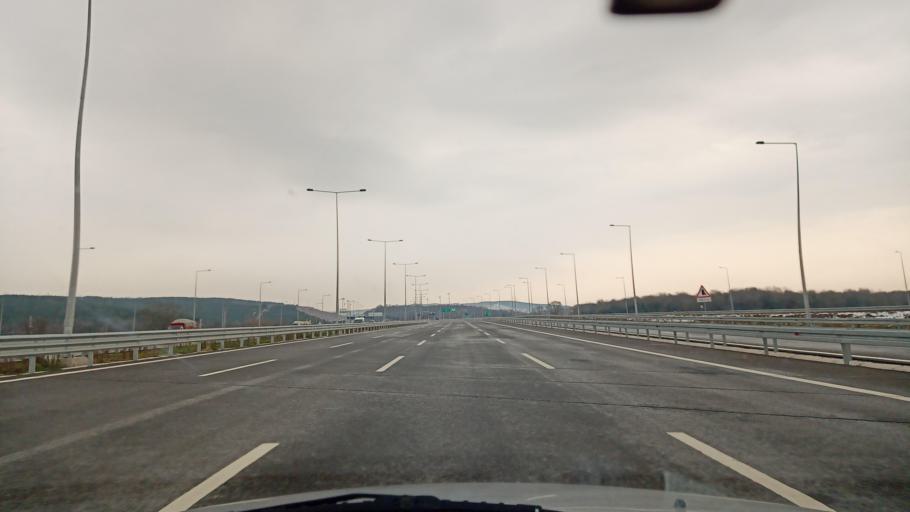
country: TR
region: Sakarya
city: Adapazari
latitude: 40.8404
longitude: 30.3553
